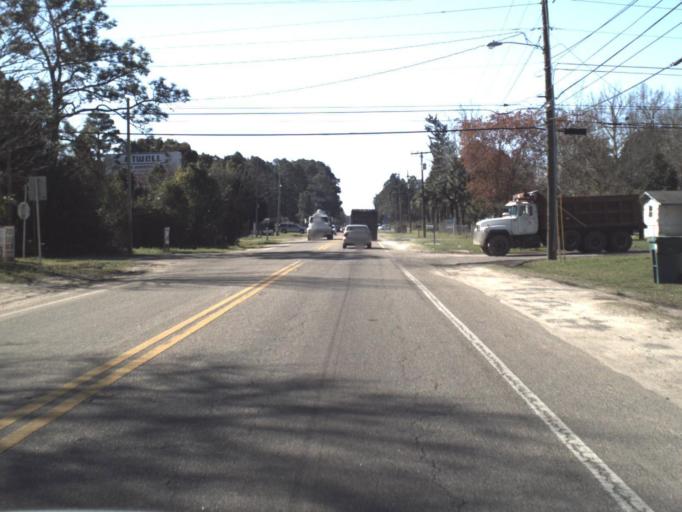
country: US
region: Florida
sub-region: Bay County
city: Hiland Park
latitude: 30.1956
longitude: -85.6250
